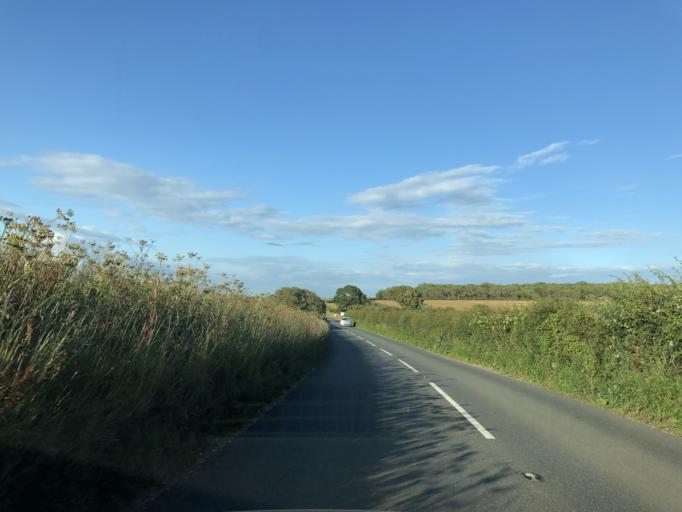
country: GB
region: England
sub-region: Isle of Wight
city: Shalfleet
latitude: 50.6730
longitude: -1.4316
